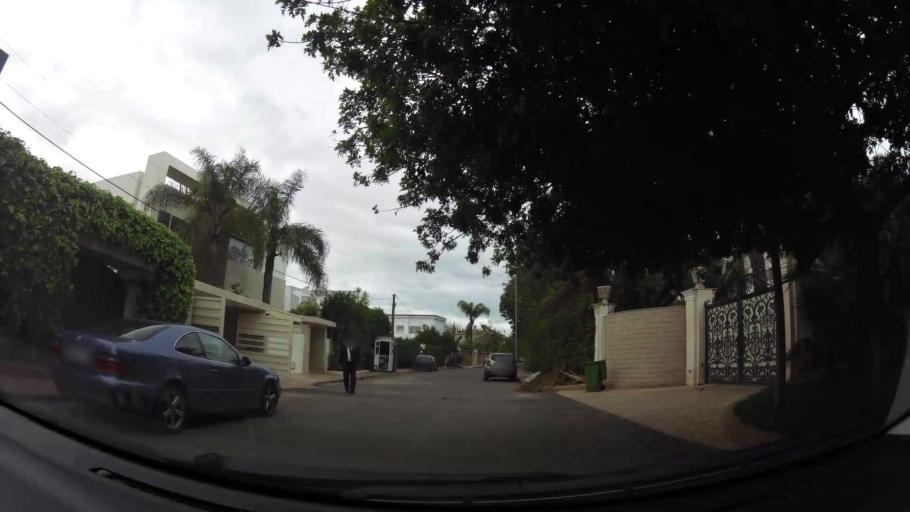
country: MA
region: Grand Casablanca
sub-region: Casablanca
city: Casablanca
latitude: 33.5813
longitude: -7.6671
